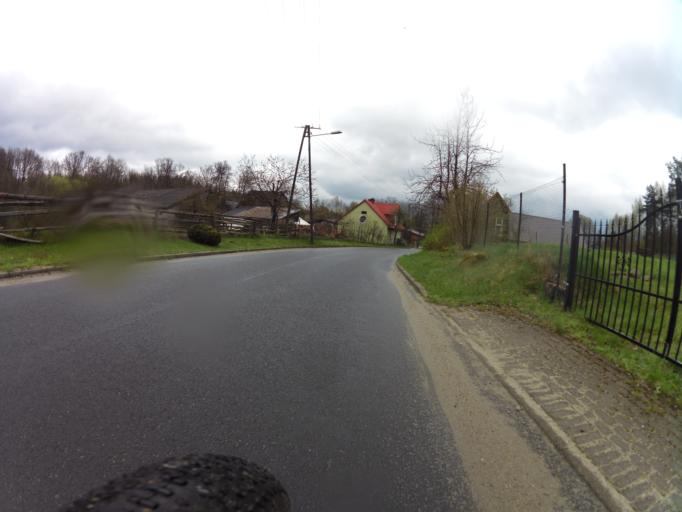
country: PL
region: Pomeranian Voivodeship
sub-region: Powiat slupski
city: Kepice
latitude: 54.2826
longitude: 16.8098
